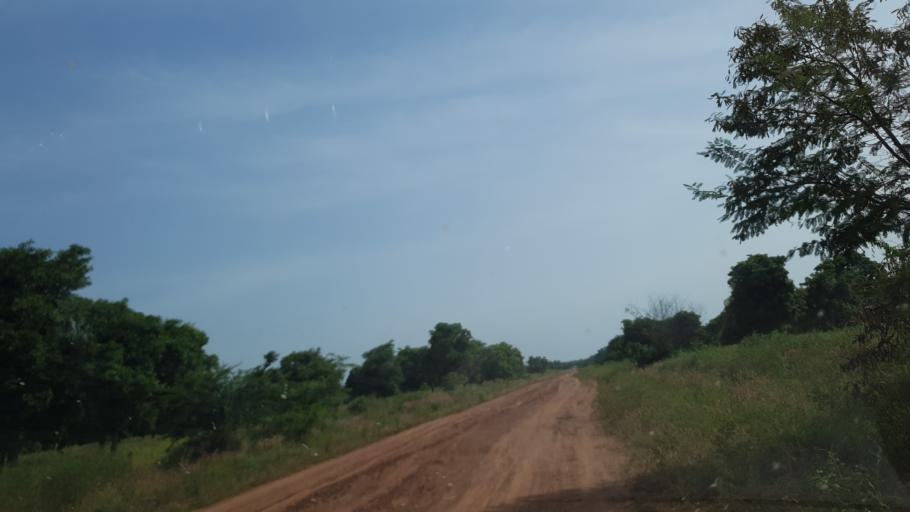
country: ML
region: Koulikoro
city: Dioila
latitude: 12.4186
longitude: -6.2324
